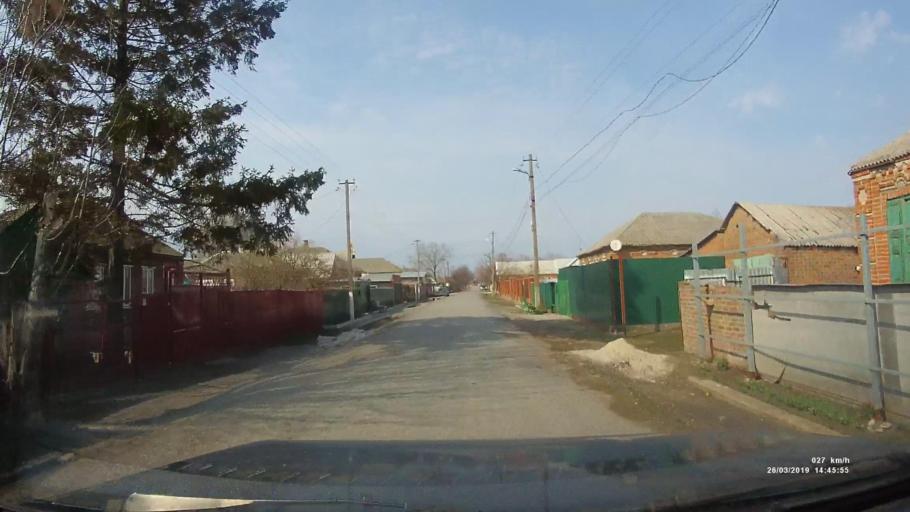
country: RU
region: Rostov
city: Novobessergenovka
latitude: 47.1843
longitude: 38.8610
